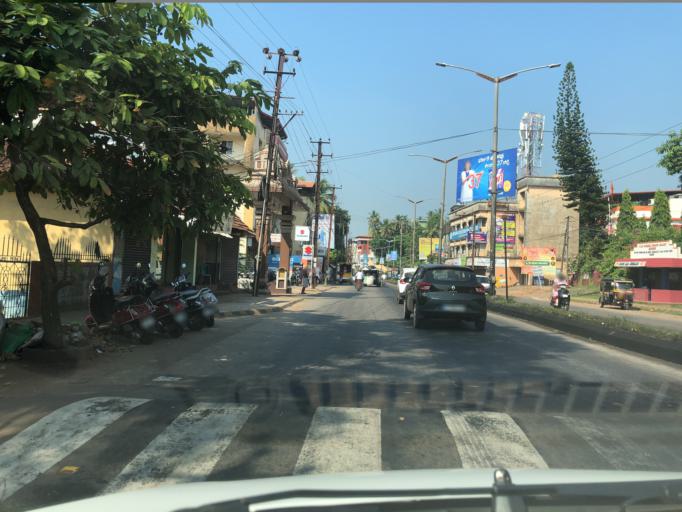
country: IN
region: Karnataka
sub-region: Dakshina Kannada
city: Mangalore
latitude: 12.8937
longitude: 74.8358
